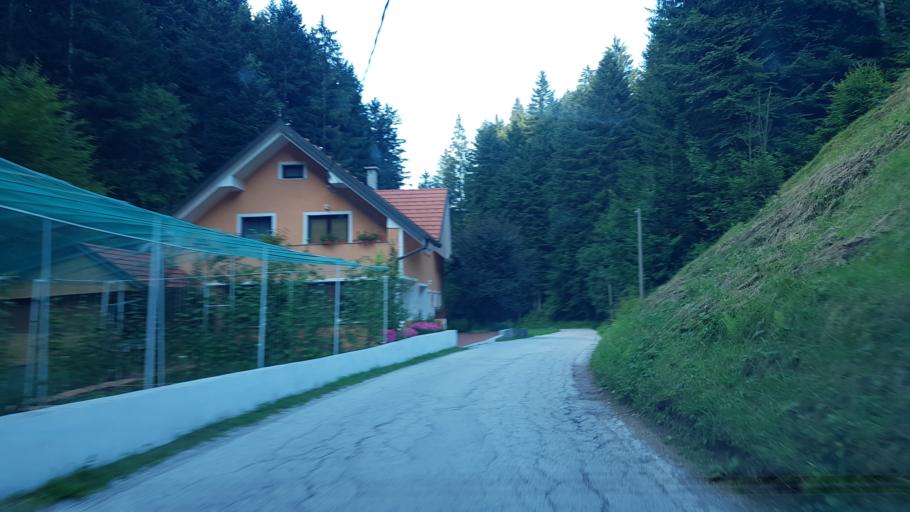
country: SI
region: Idrija
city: Spodnja Idrija
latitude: 46.0818
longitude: 14.0321
